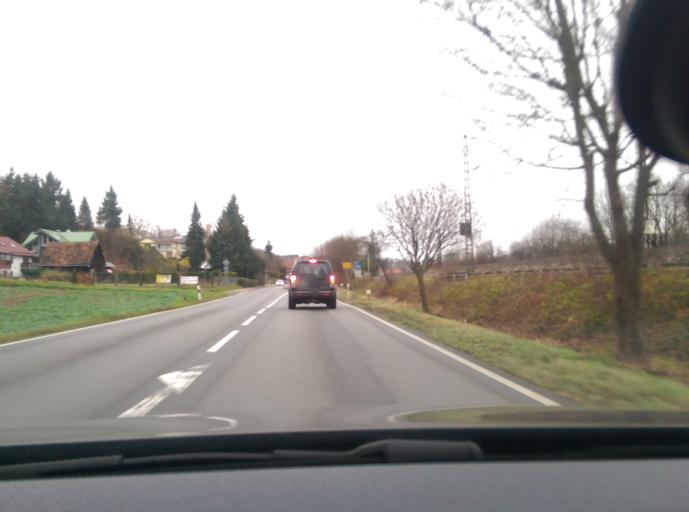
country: DE
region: Hesse
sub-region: Regierungsbezirk Kassel
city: Eschwege
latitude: 51.1756
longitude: 9.9888
